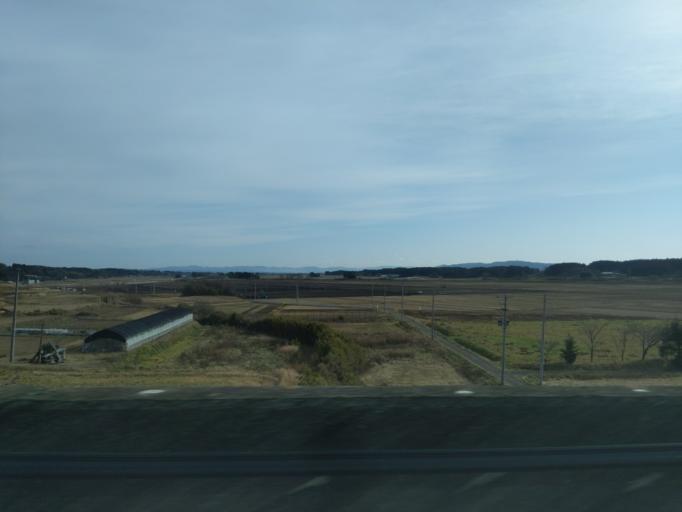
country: JP
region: Miyagi
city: Furukawa
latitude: 38.6558
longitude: 141.0190
